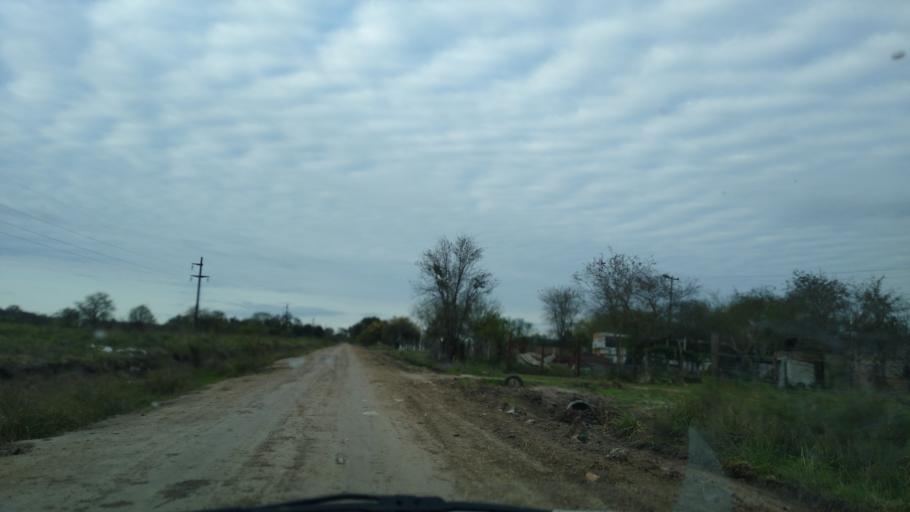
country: AR
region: Chaco
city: Fontana
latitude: -27.3853
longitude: -59.0440
